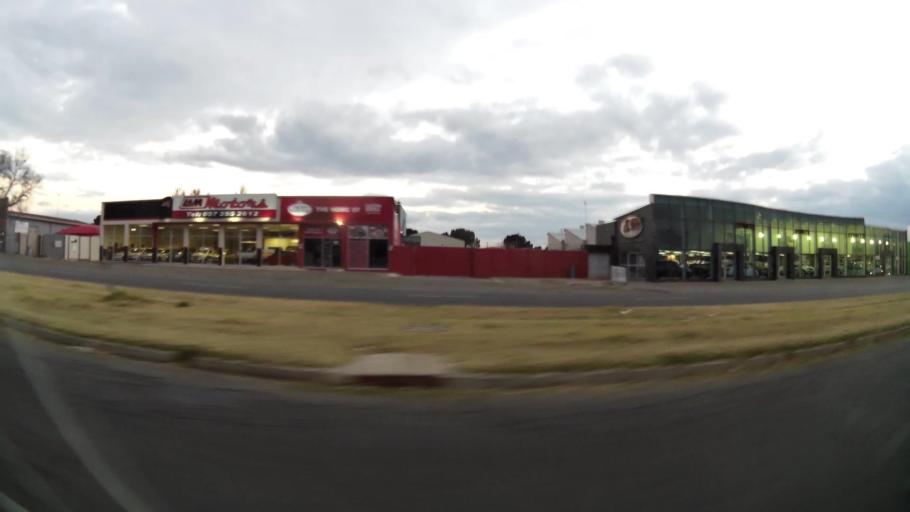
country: ZA
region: Orange Free State
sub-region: Lejweleputswa District Municipality
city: Welkom
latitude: -27.9812
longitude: 26.7666
